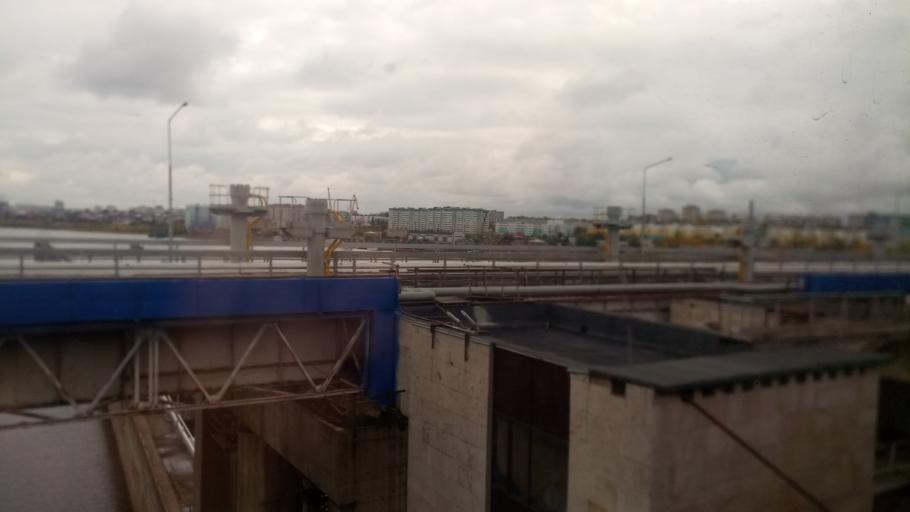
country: RU
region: Tatarstan
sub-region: Tukayevskiy Rayon
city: Naberezhnyye Chelny
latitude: 55.6945
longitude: 52.2794
